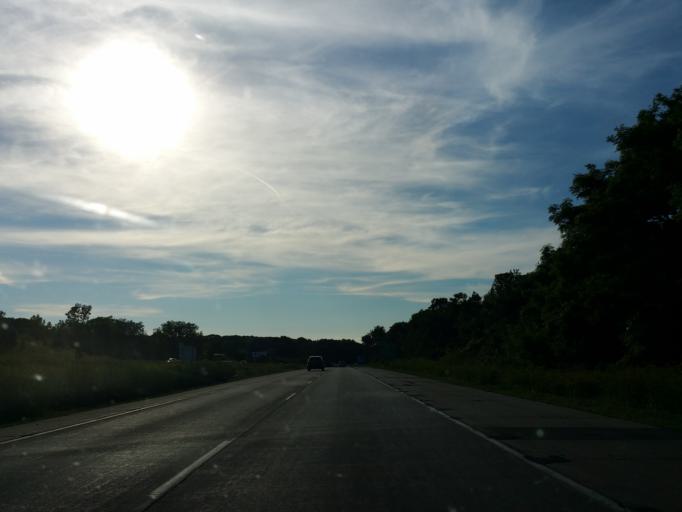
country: US
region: Wisconsin
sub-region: Columbia County
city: Portage
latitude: 43.5017
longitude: -89.5091
